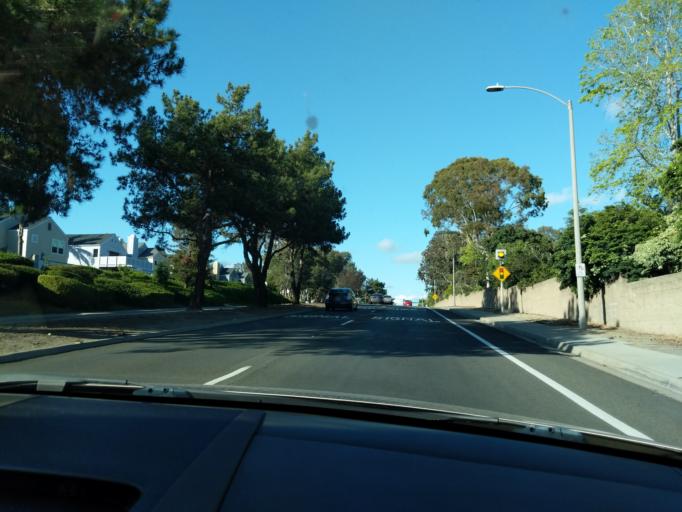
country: US
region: California
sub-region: San Diego County
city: Lake San Marcos
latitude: 33.1208
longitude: -117.2201
